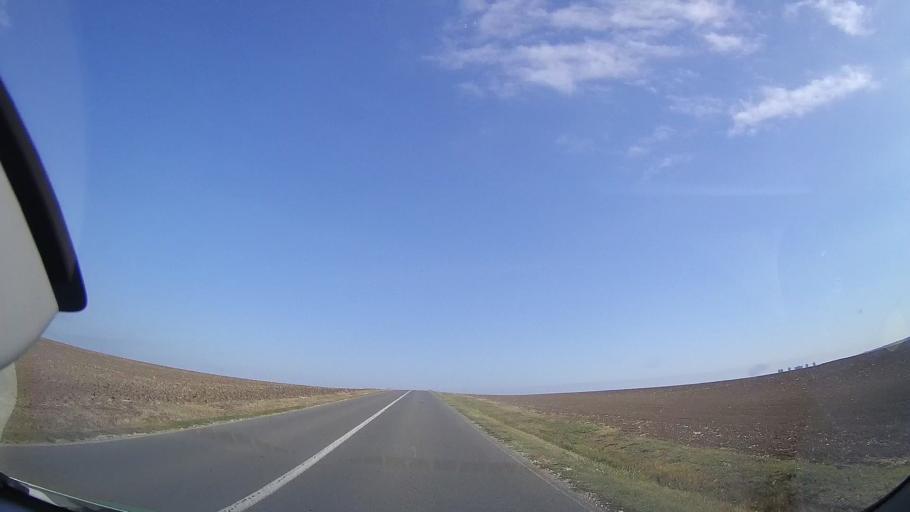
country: RO
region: Constanta
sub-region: Comuna Douazeci si Trei August
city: Douazeci si Trei August
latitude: 43.9138
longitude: 28.5650
